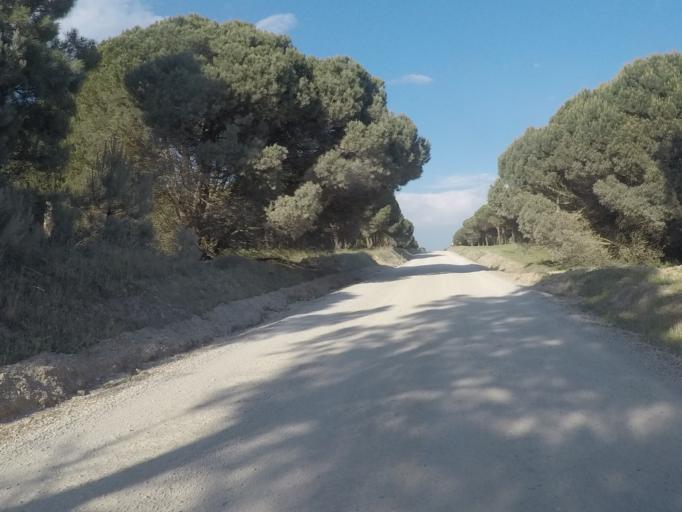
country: PT
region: Setubal
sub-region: Sesimbra
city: Sesimbra
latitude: 38.4532
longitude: -9.1946
